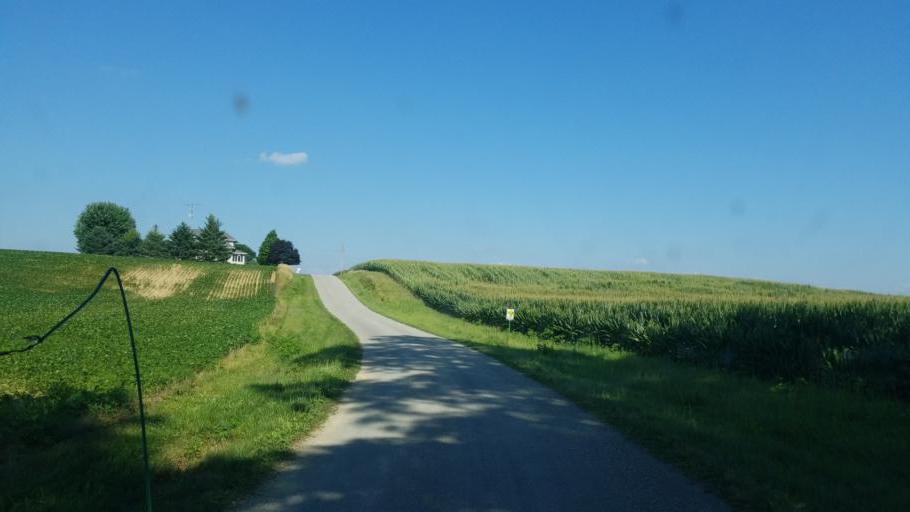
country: US
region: Ohio
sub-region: Wyandot County
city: Upper Sandusky
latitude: 40.7888
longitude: -83.3311
